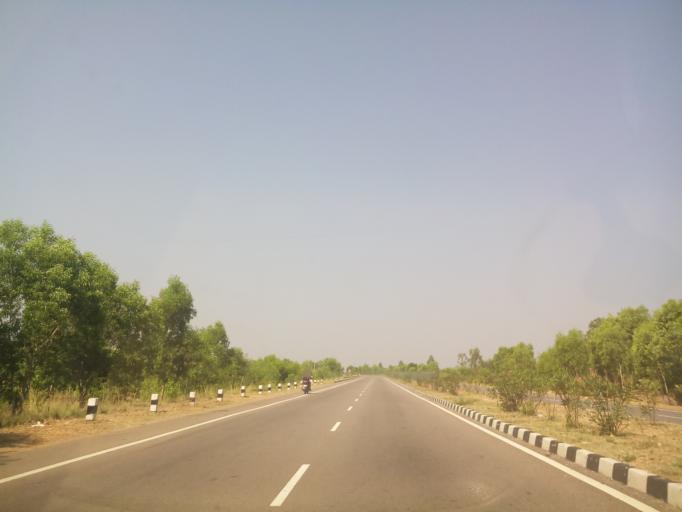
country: IN
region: Karnataka
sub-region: Mandya
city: Belluru
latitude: 12.9786
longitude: 76.8330
